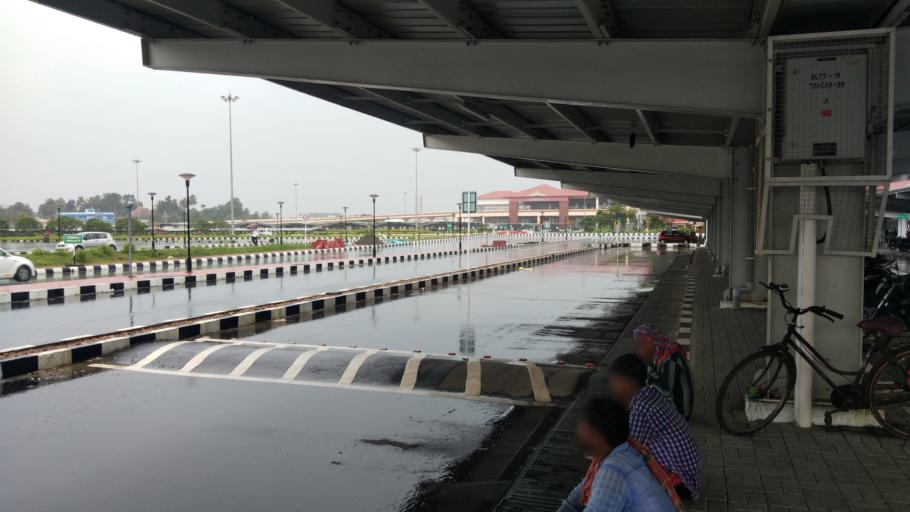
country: IN
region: Kerala
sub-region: Ernakulam
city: Angamali
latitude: 10.1570
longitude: 76.3898
